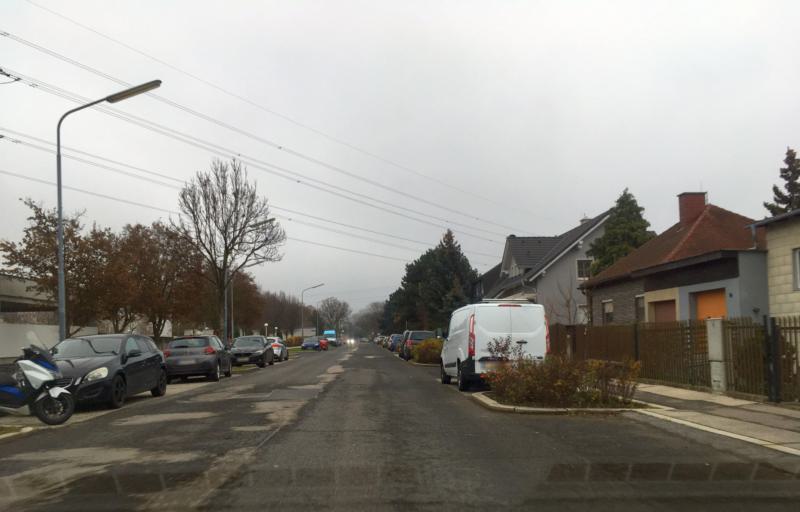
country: AT
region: Lower Austria
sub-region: Politischer Bezirk Wien-Umgebung
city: Gerasdorf bei Wien
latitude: 48.2151
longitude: 16.4689
